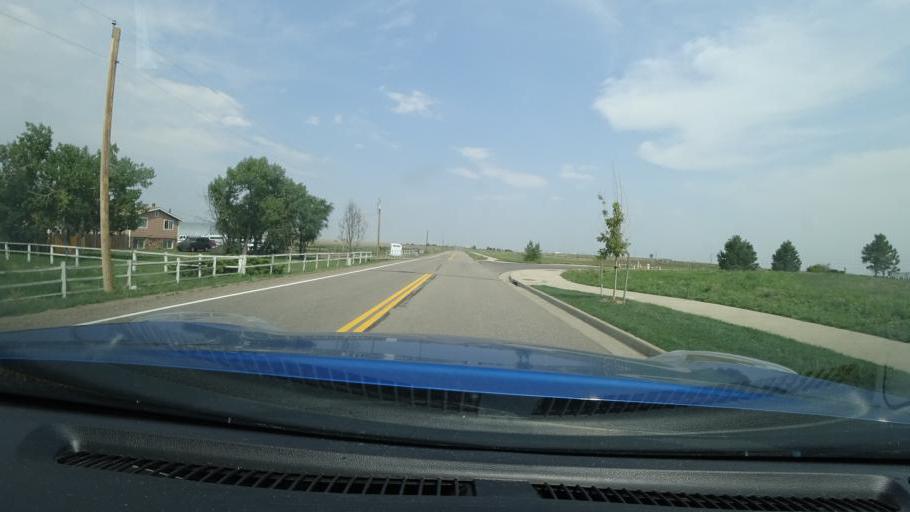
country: US
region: Colorado
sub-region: Adams County
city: Aurora
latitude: 39.7547
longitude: -104.7293
